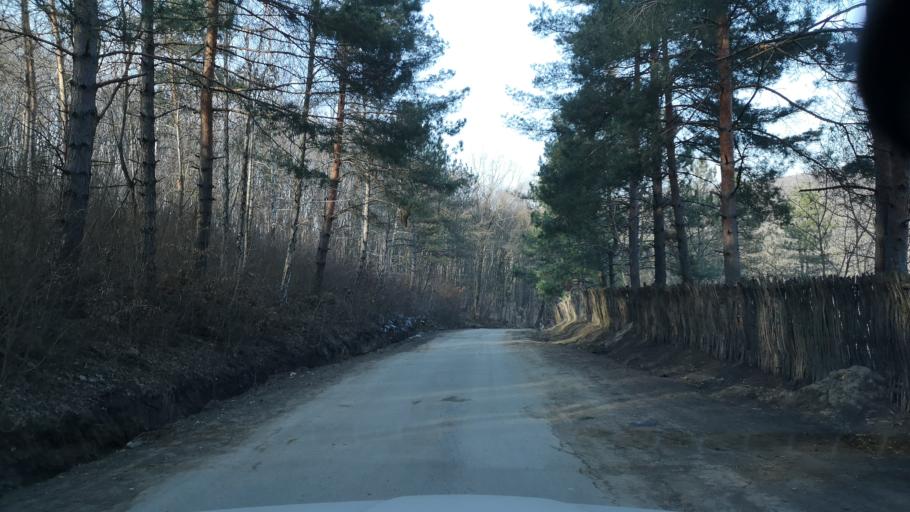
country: MD
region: Nisporeni
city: Nisporeni
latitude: 47.0814
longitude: 28.3221
